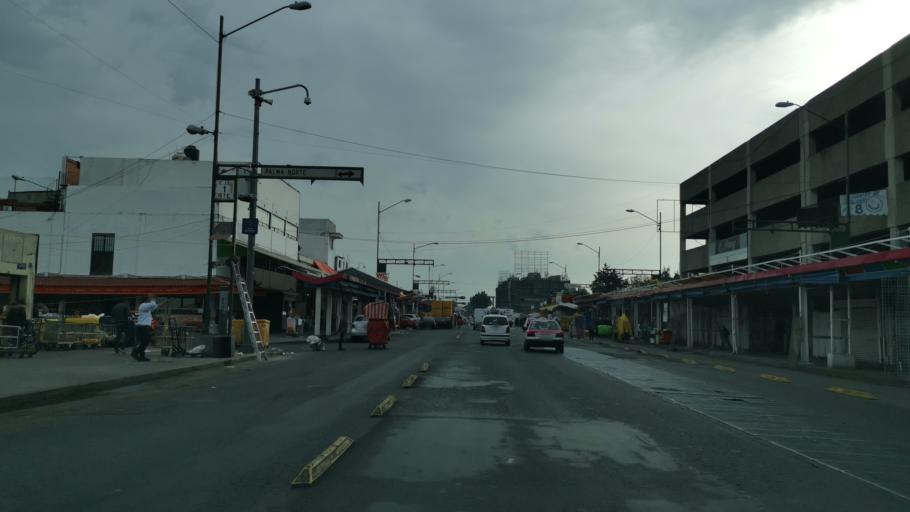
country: MX
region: Mexico City
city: Cuauhtemoc
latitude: 19.4436
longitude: -99.1342
